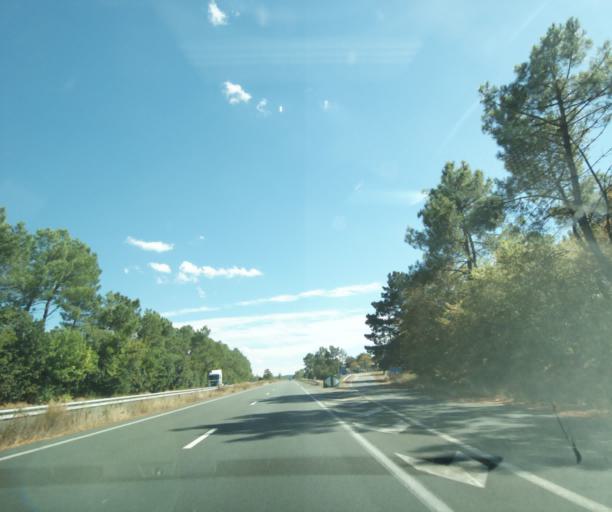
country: FR
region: Aquitaine
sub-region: Departement du Lot-et-Garonne
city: Buzet-sur-Baise
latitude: 44.2512
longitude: 0.2988
